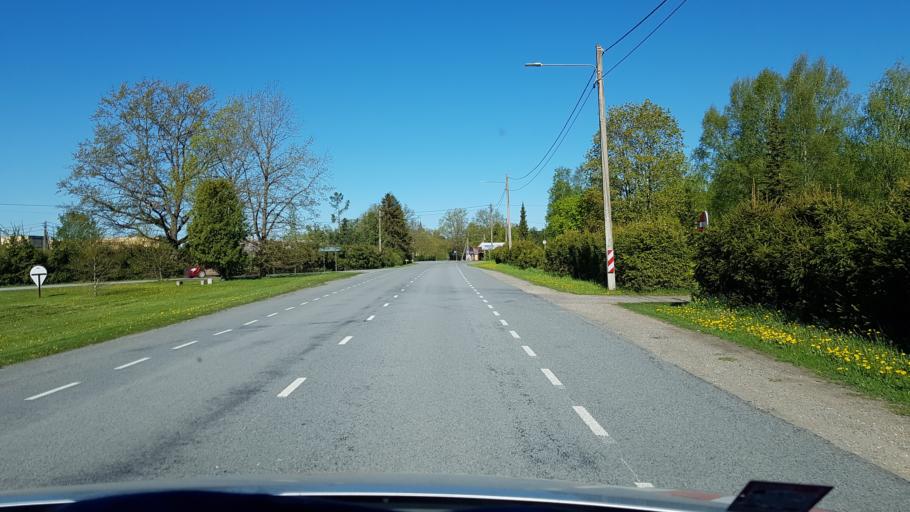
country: EE
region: Polvamaa
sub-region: Polva linn
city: Polva
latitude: 58.2823
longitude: 27.0525
